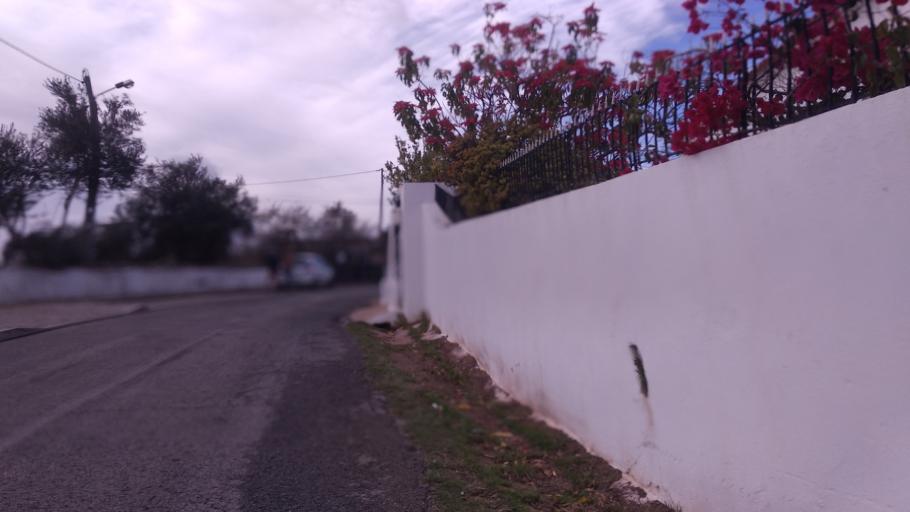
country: PT
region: Faro
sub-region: Sao Bras de Alportel
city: Sao Bras de Alportel
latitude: 37.1756
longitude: -7.9078
